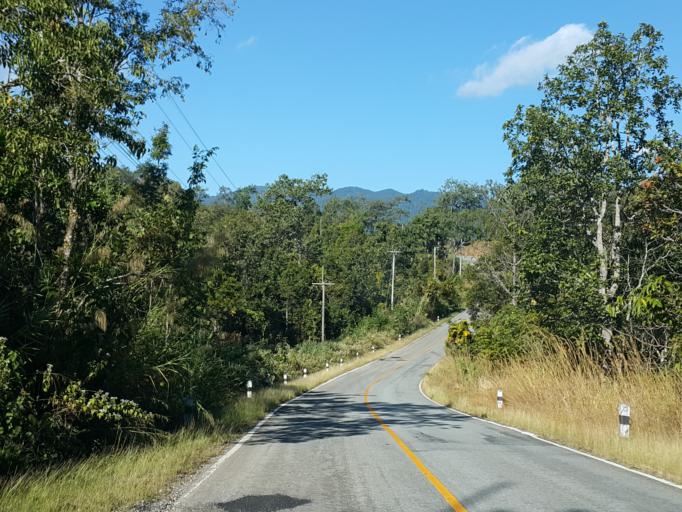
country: TH
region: Chiang Mai
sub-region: Amphoe Chiang Dao
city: Chiang Dao
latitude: 19.5268
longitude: 98.8930
